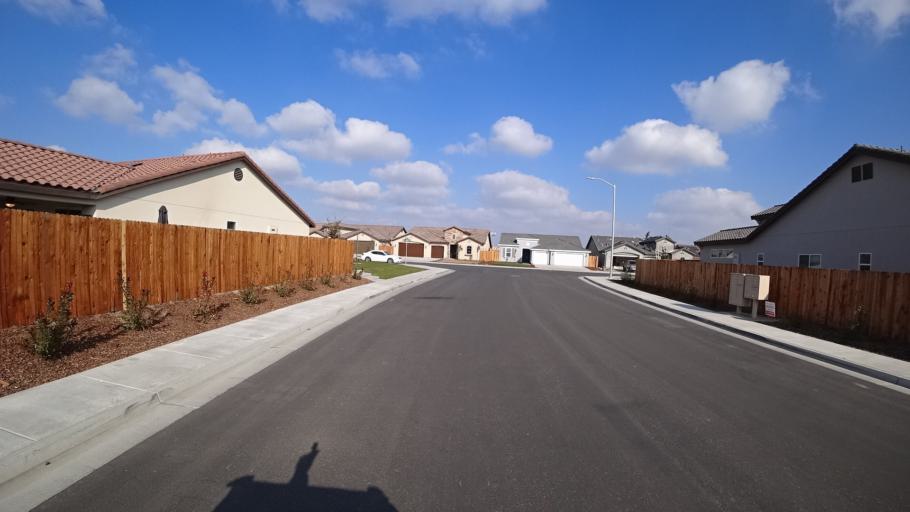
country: US
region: California
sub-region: Kern County
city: Greenacres
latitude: 35.2907
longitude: -119.1046
